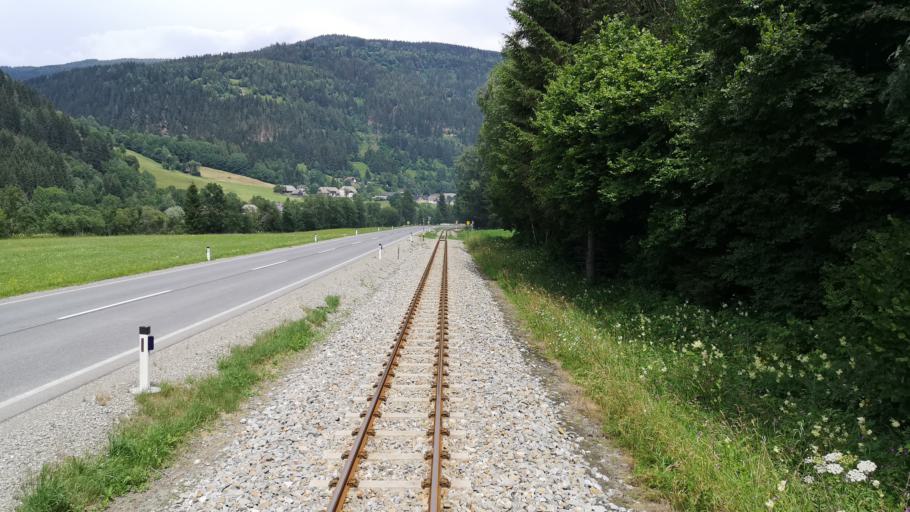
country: AT
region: Styria
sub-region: Politischer Bezirk Murau
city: Stadl an der Mur
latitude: 47.0823
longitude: 13.9337
